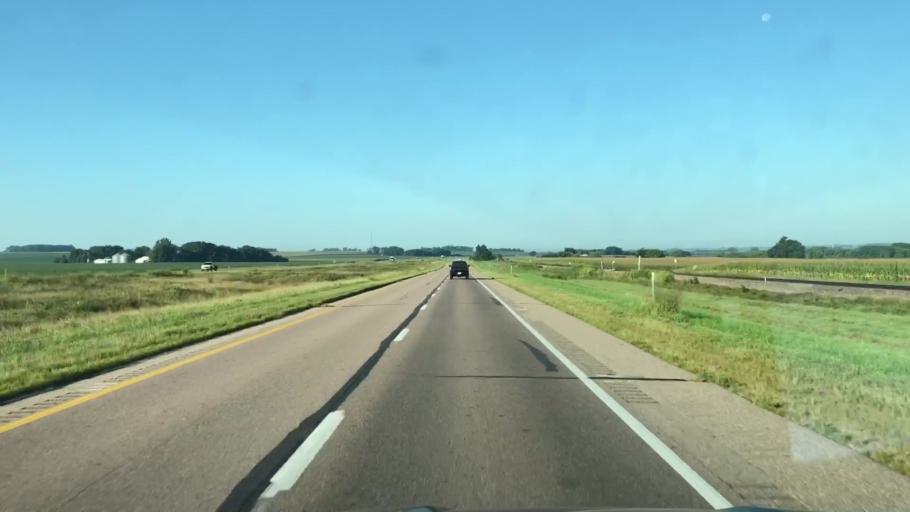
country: US
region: Iowa
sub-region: Sioux County
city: Alton
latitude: 43.0186
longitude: -95.9566
